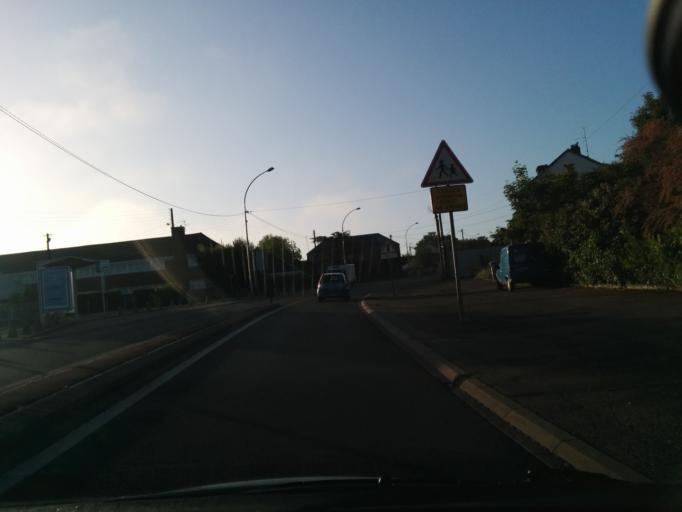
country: FR
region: Ile-de-France
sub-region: Departement des Yvelines
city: Freneuse
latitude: 49.0379
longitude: 1.5958
